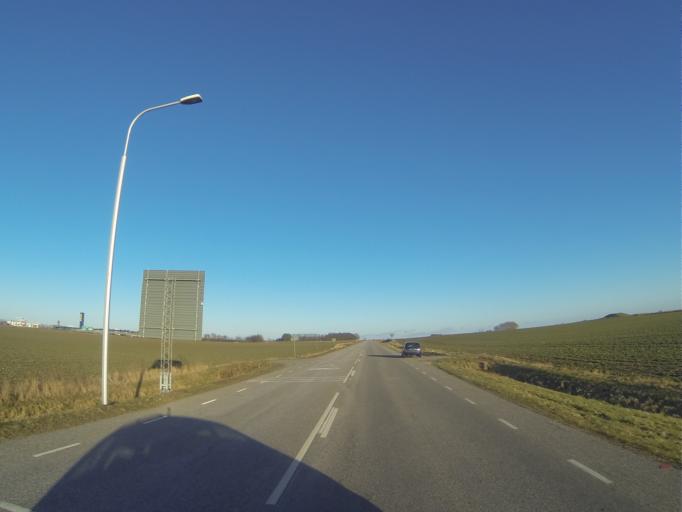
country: SE
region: Skane
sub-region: Malmo
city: Tygelsjo
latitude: 55.5450
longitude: 12.9829
